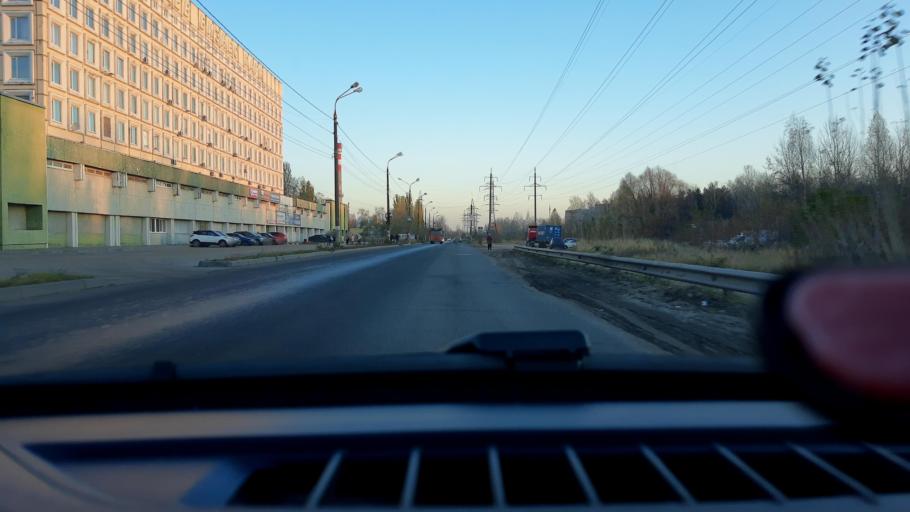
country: RU
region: Nizjnij Novgorod
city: Gorbatovka
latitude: 56.3656
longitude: 43.7951
